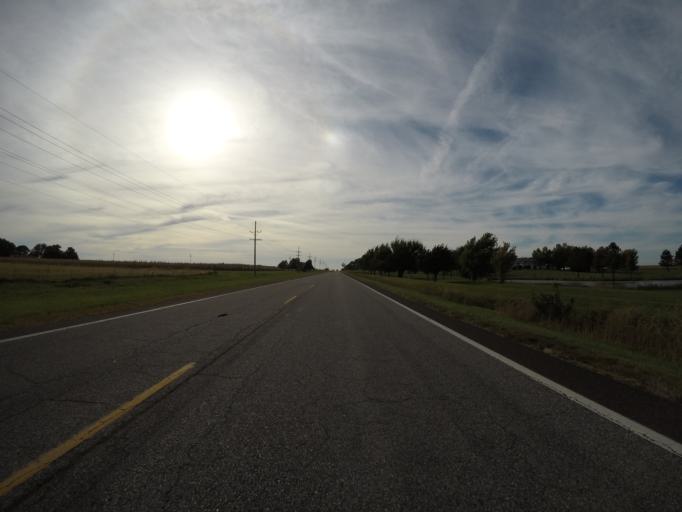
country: US
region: Kansas
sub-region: Franklin County
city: Wellsville
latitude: 38.7678
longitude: -95.1097
